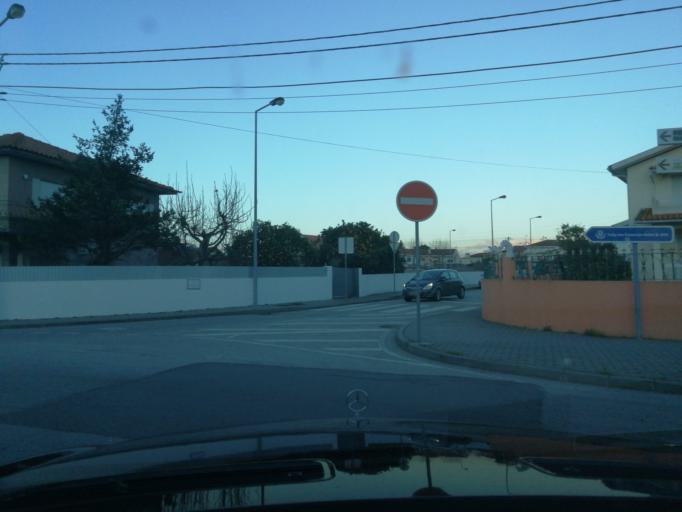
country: PT
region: Aveiro
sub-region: Estarreja
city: Estarreja
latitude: 40.7563
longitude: -8.5753
